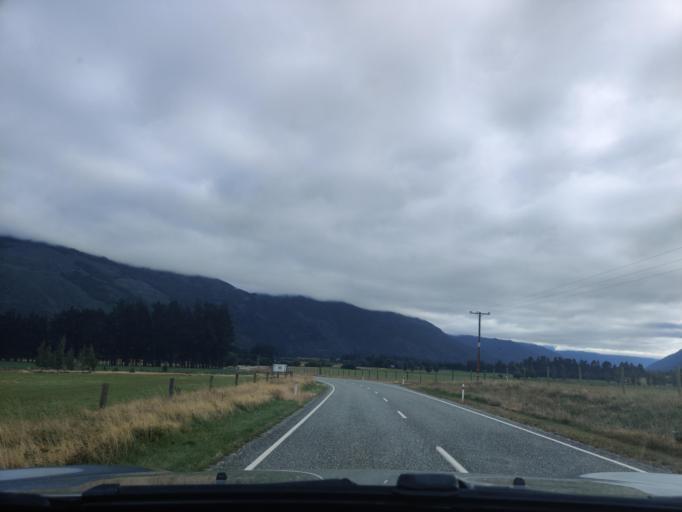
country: NZ
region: Otago
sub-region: Queenstown-Lakes District
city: Wanaka
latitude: -44.2748
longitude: 169.2015
